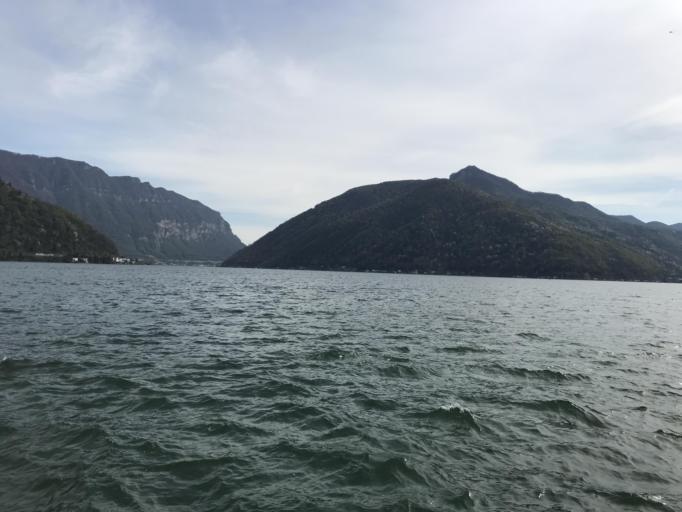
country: CH
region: Ticino
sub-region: Lugano District
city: Melide
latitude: 45.9525
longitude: 8.9548
